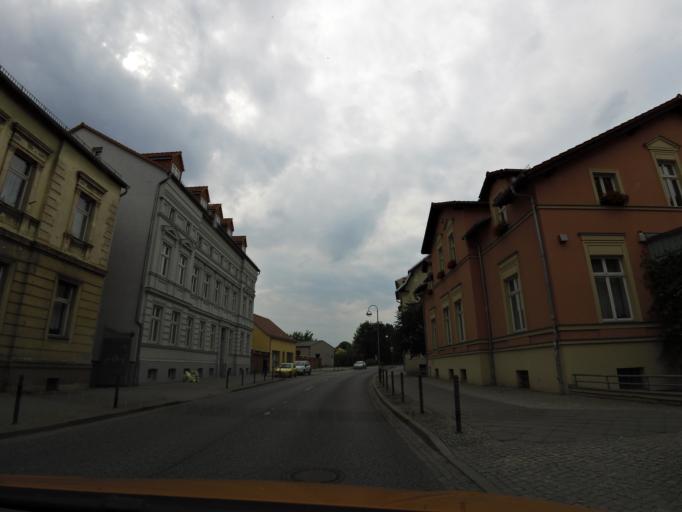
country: DE
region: Brandenburg
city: Zossen
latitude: 52.2150
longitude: 13.4446
